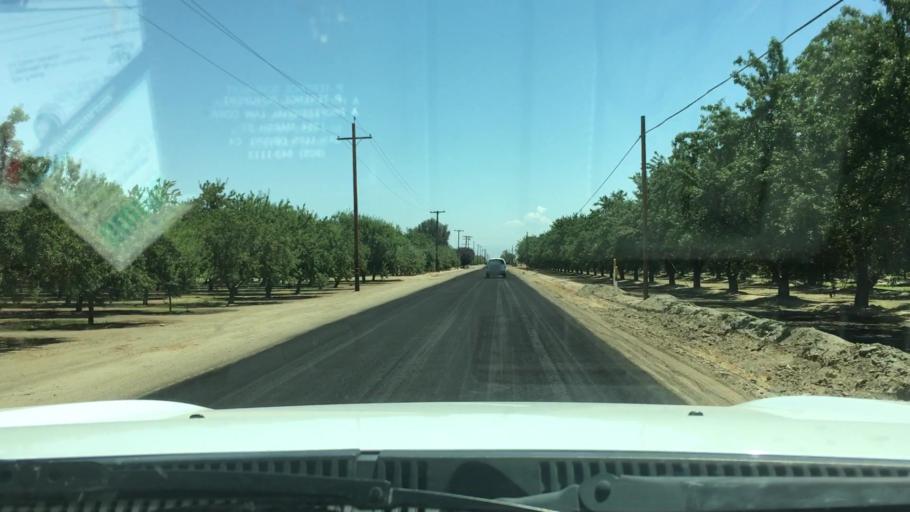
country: US
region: California
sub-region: Kern County
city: Shafter
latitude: 35.5291
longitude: -119.3212
